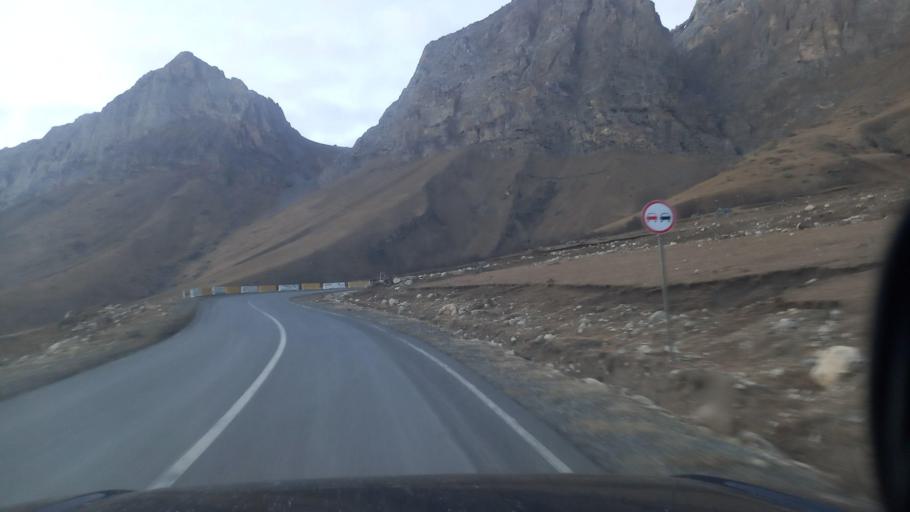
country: RU
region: Ingushetiya
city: Dzhayrakh
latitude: 42.8244
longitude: 44.8245
